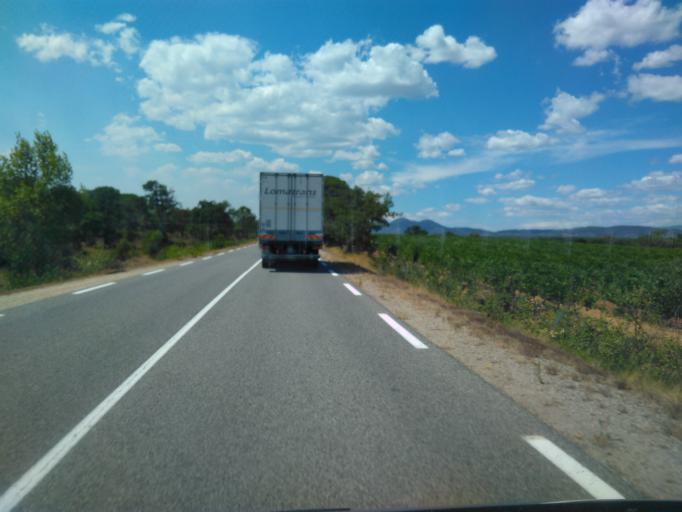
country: FR
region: Provence-Alpes-Cote d'Azur
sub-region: Departement du Var
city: La Garde-Freinet
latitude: 43.3567
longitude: 6.4069
